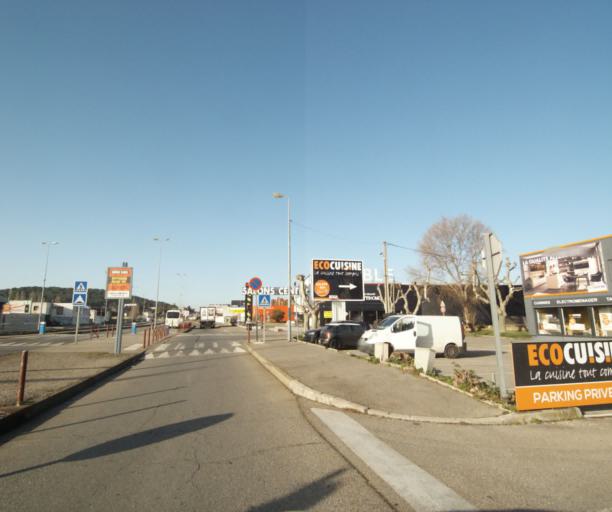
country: FR
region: Provence-Alpes-Cote d'Azur
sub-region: Departement des Bouches-du-Rhone
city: Septemes-les-Vallons
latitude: 43.4168
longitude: 5.3550
